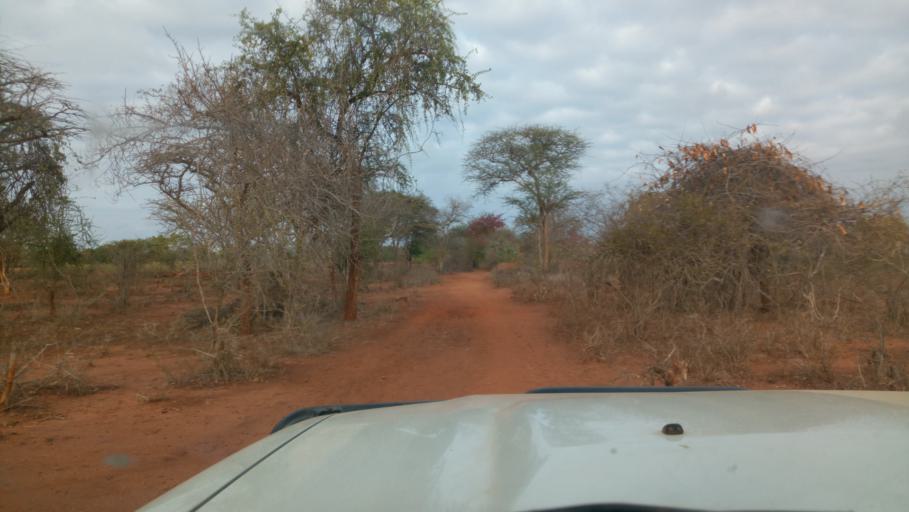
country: KE
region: Kitui
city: Kitui
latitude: -1.8941
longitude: 38.2293
